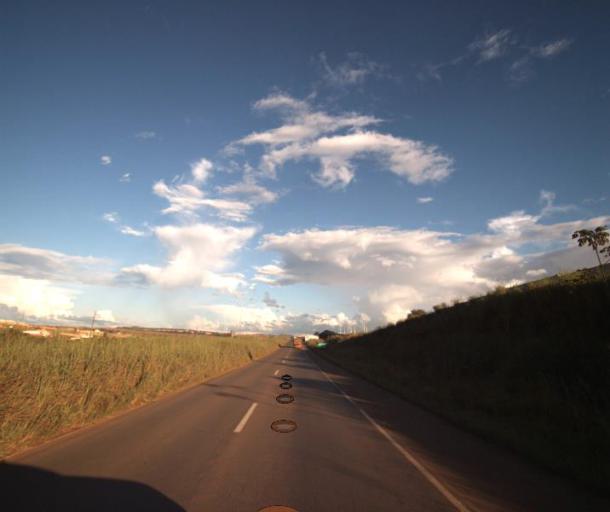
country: BR
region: Goias
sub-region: Anapolis
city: Anapolis
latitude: -16.2931
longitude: -48.9337
